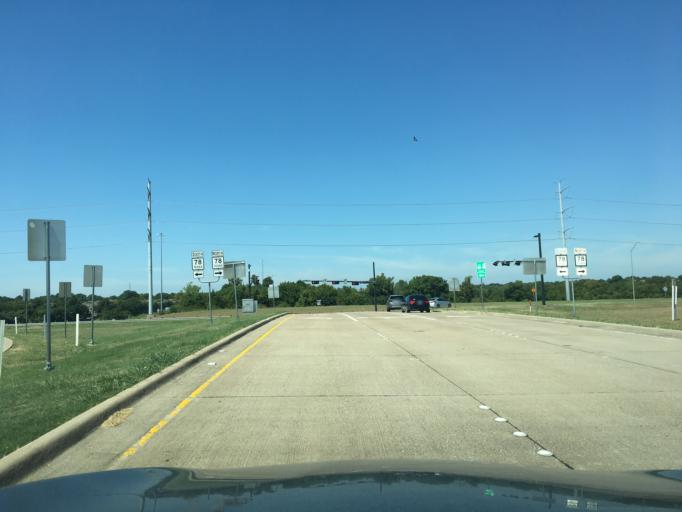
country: US
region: Texas
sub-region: Dallas County
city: Sachse
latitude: 32.9517
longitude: -96.6173
